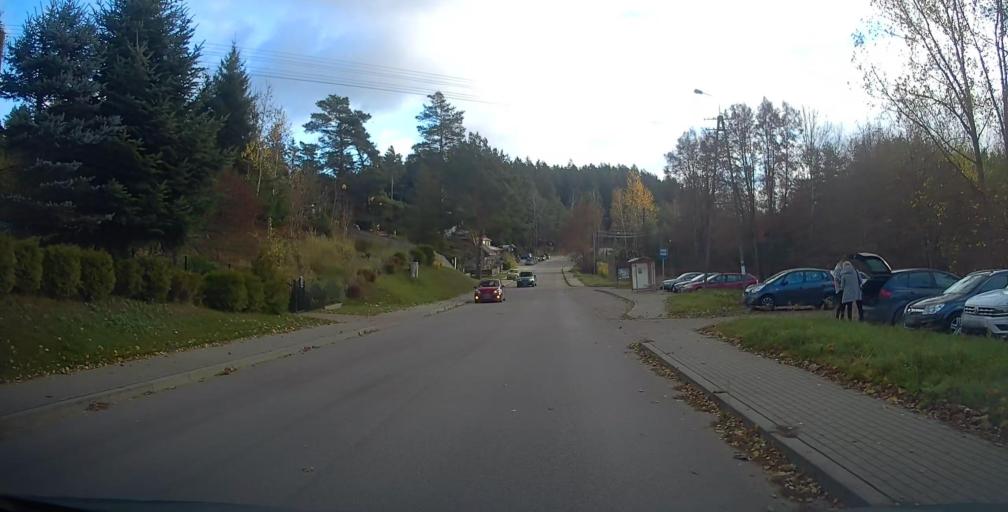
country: PL
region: Podlasie
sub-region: Suwalki
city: Suwalki
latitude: 54.2874
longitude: 22.8860
